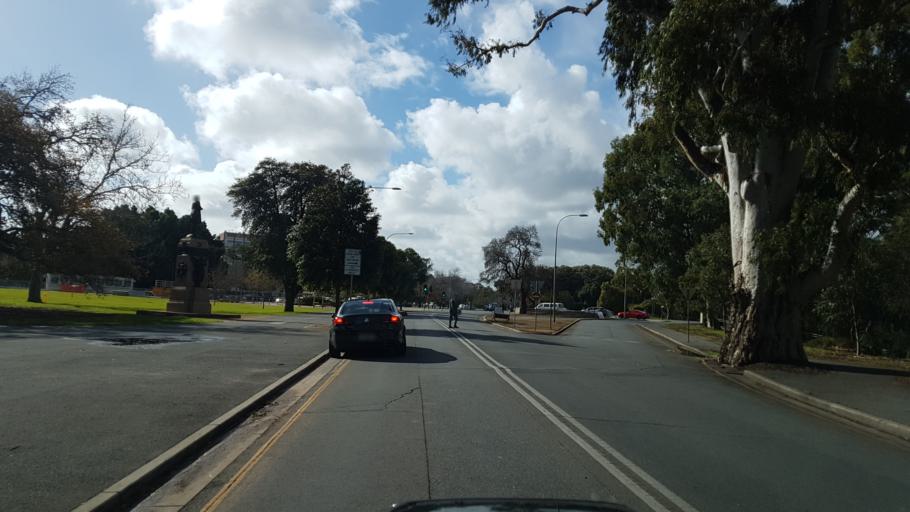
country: AU
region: South Australia
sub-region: Adelaide
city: North Adelaide
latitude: -34.9164
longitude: 138.5977
